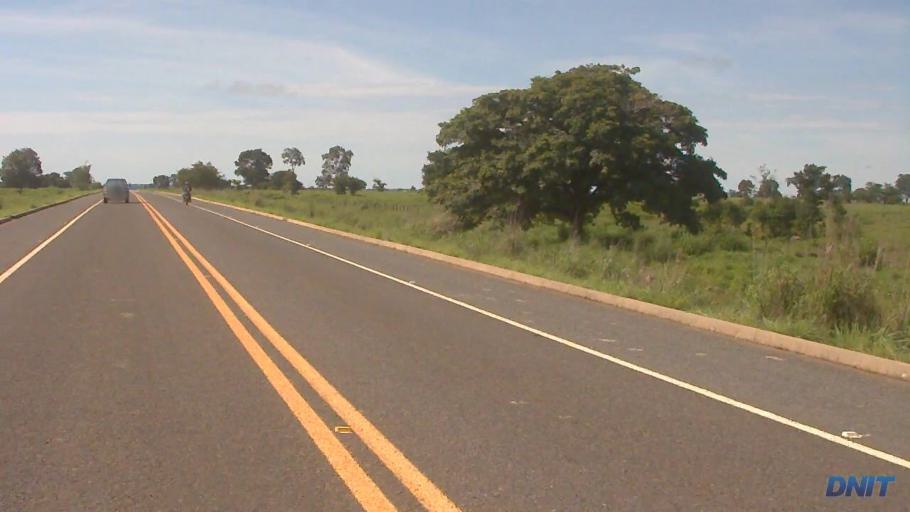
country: BR
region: Goias
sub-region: Sao Miguel Do Araguaia
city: Sao Miguel do Araguaia
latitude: -13.4592
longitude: -50.1182
